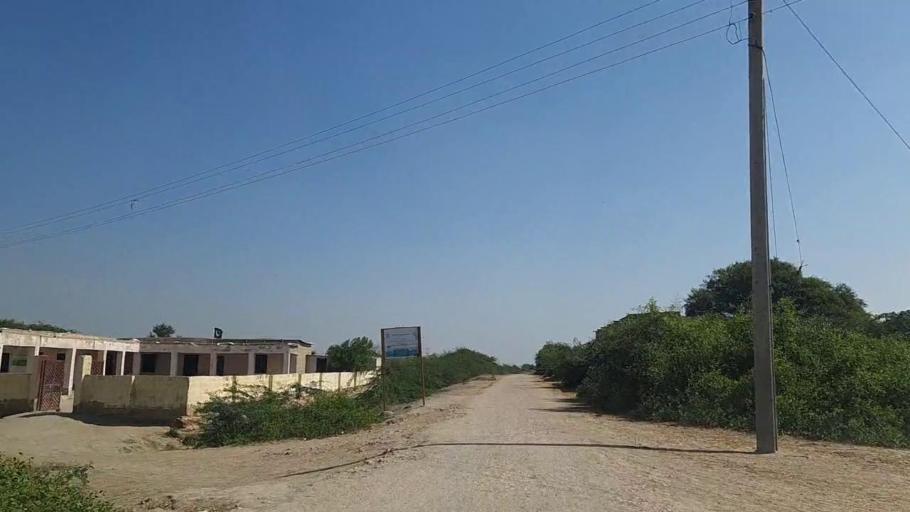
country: PK
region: Sindh
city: Daro Mehar
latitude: 24.7167
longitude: 68.1625
